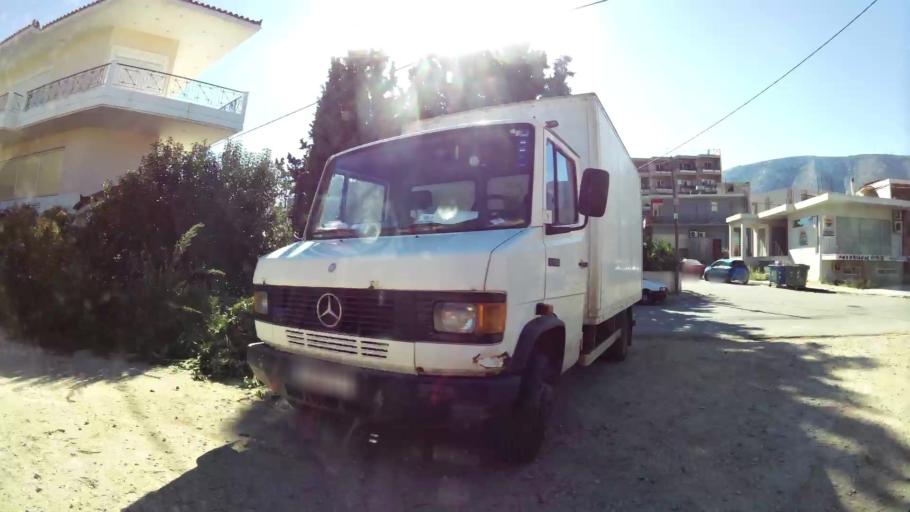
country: GR
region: Attica
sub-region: Nomarchia Anatolikis Attikis
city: Paiania
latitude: 37.9594
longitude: 23.8573
